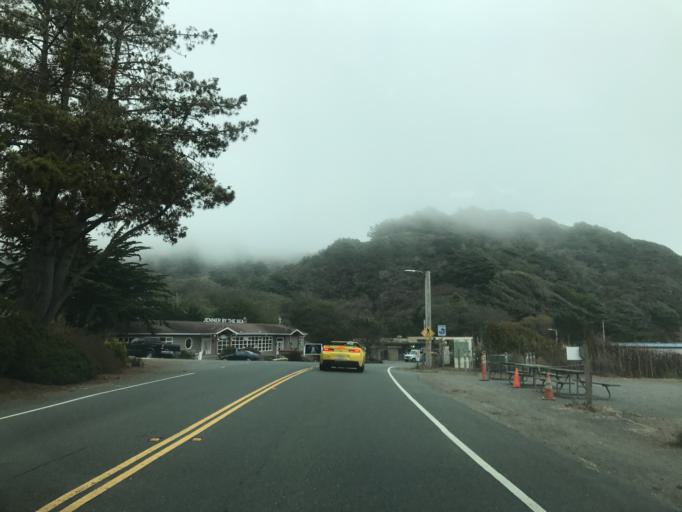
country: US
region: California
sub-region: Sonoma County
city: Monte Rio
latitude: 38.4500
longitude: -123.1160
